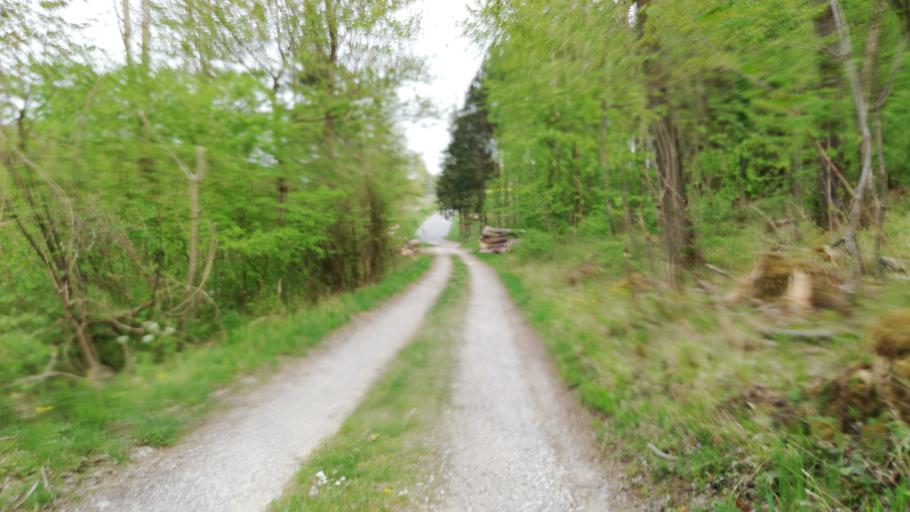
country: AT
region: Upper Austria
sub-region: Wels-Land
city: Gunskirchen
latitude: 48.1850
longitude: 13.9603
